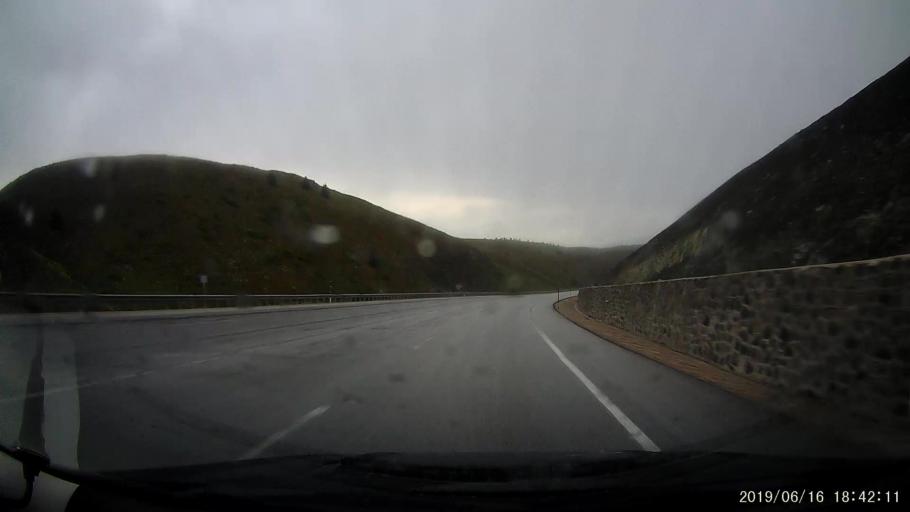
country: TR
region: Erzincan
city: Doganbeyli
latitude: 39.8704
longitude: 39.1149
